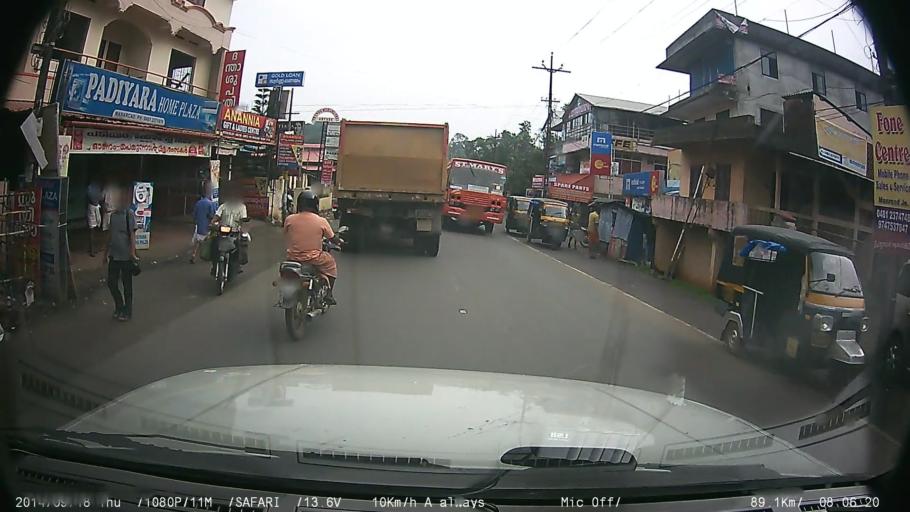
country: IN
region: Kerala
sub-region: Kottayam
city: Kottayam
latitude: 9.5883
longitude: 76.5827
